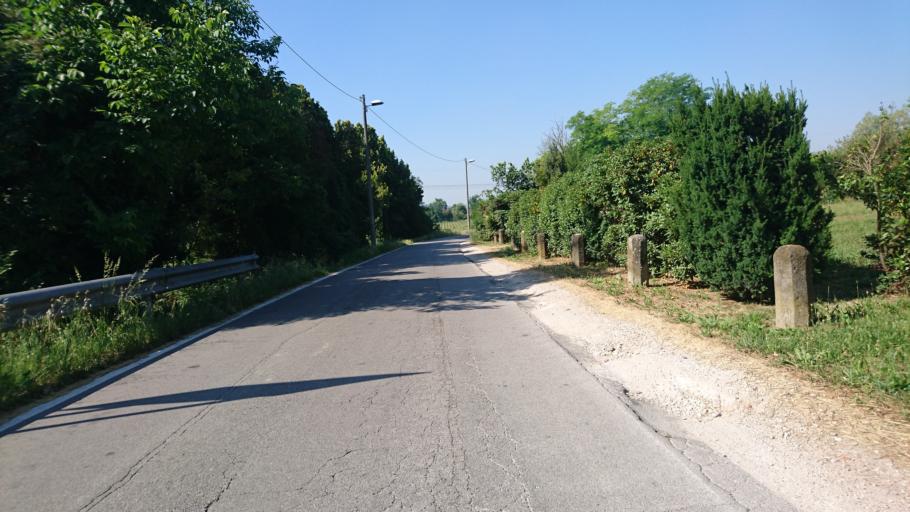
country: IT
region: Veneto
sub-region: Provincia di Padova
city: Tencarola
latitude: 45.3726
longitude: 11.8122
